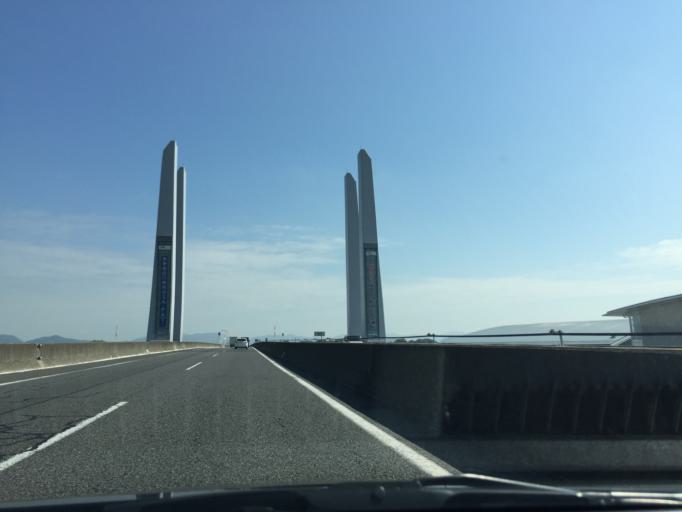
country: JP
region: Aichi
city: Kuroda
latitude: 35.3579
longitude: 136.7979
